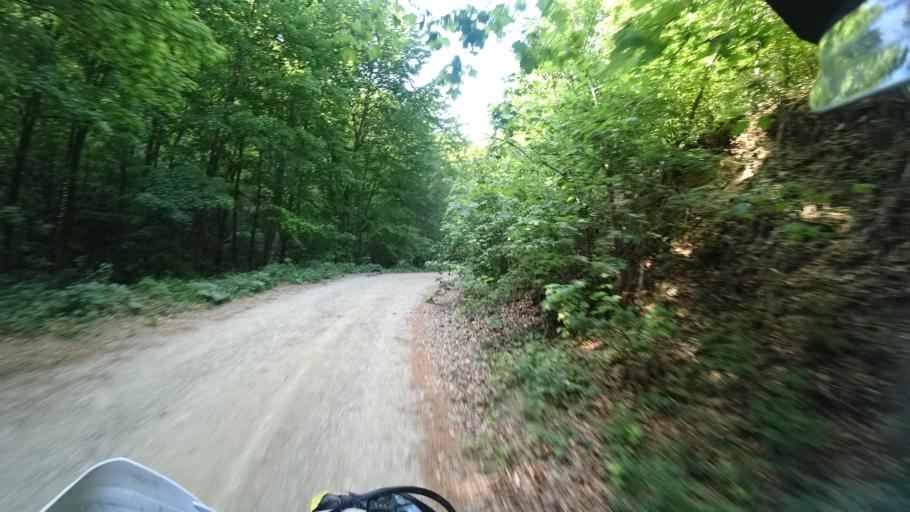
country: HR
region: Zagrebacka
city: Jablanovec
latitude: 45.8585
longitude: 15.8907
